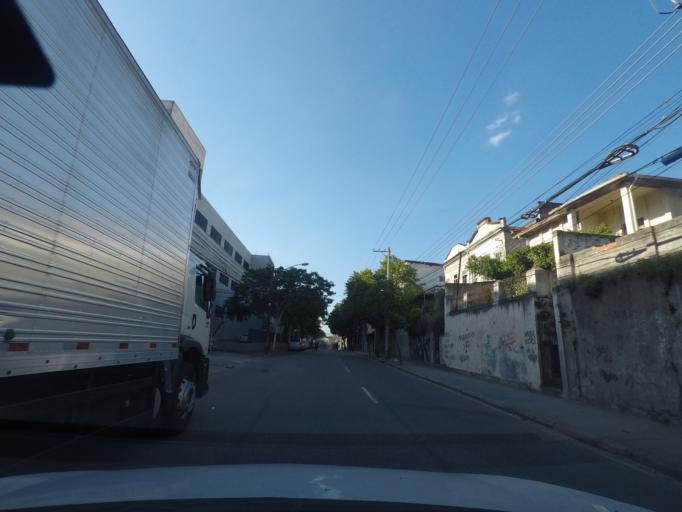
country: BR
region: Rio de Janeiro
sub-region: Rio De Janeiro
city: Rio de Janeiro
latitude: -22.8972
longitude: -43.2263
